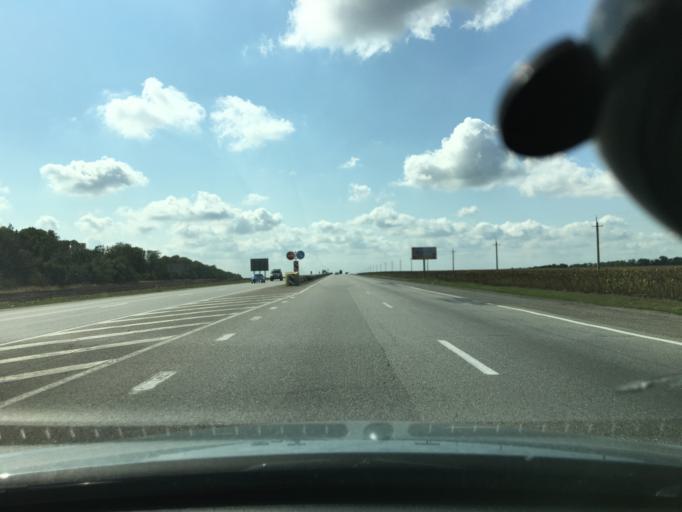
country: RU
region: Krasnodarskiy
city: Krasnoye
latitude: 46.7506
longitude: 39.6596
